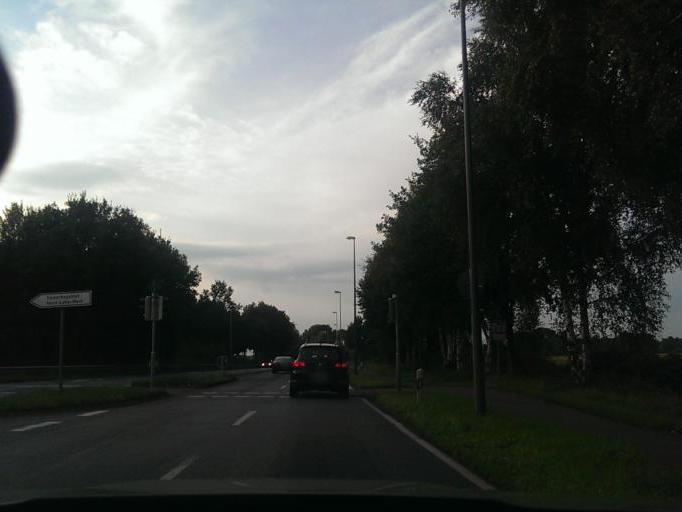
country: DE
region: Lower Saxony
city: Lilienthal
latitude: 53.1124
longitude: 8.8800
